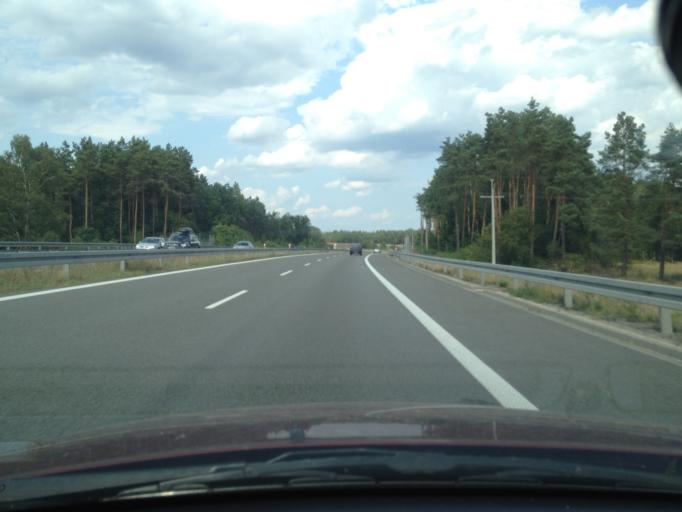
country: PL
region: West Pomeranian Voivodeship
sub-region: Powiat goleniowski
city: Goleniow
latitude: 53.6170
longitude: 14.8176
